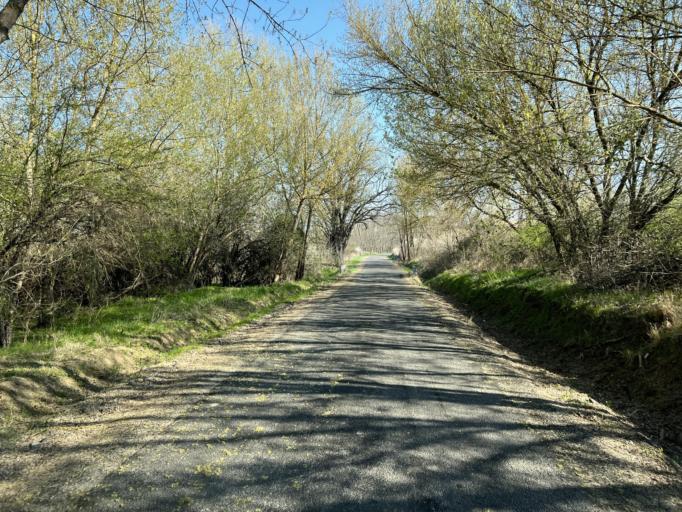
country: SK
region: Nitriansky
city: Sahy
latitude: 48.0252
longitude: 18.8277
